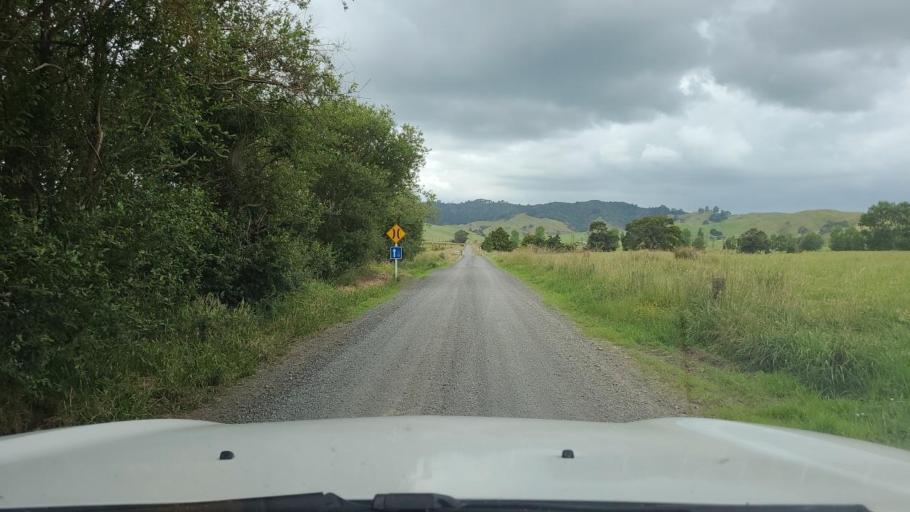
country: NZ
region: Waikato
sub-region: Hamilton City
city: Hamilton
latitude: -37.5720
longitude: 175.4112
